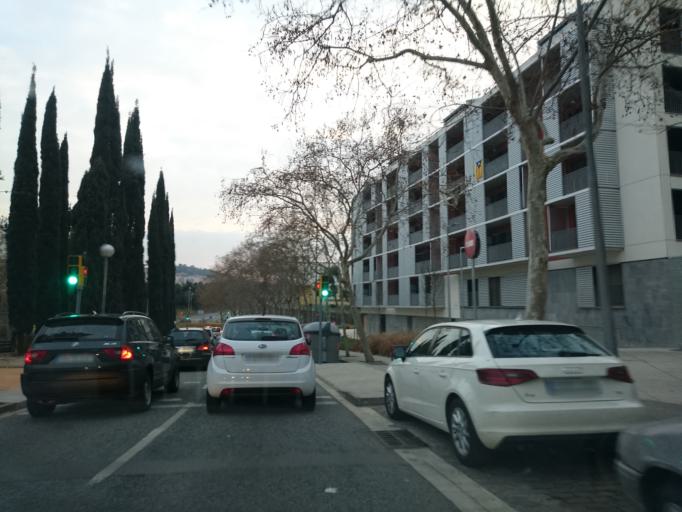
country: ES
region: Catalonia
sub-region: Provincia de Barcelona
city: Horta-Guinardo
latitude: 41.4348
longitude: 2.1530
